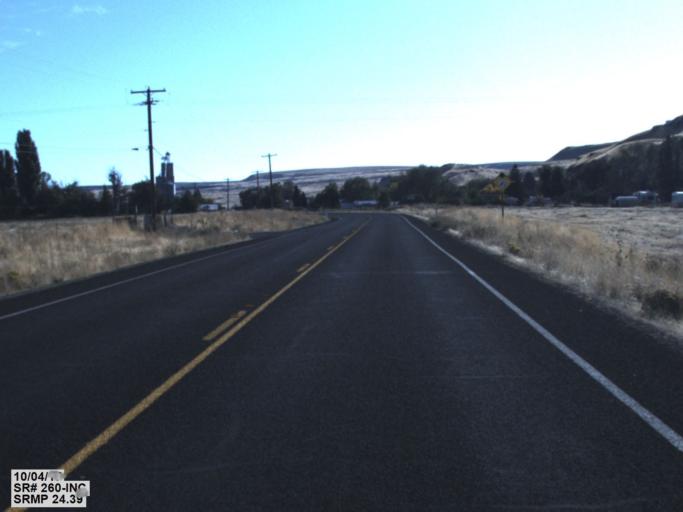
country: US
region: Washington
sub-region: Franklin County
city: Connell
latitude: 46.6431
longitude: -118.5651
